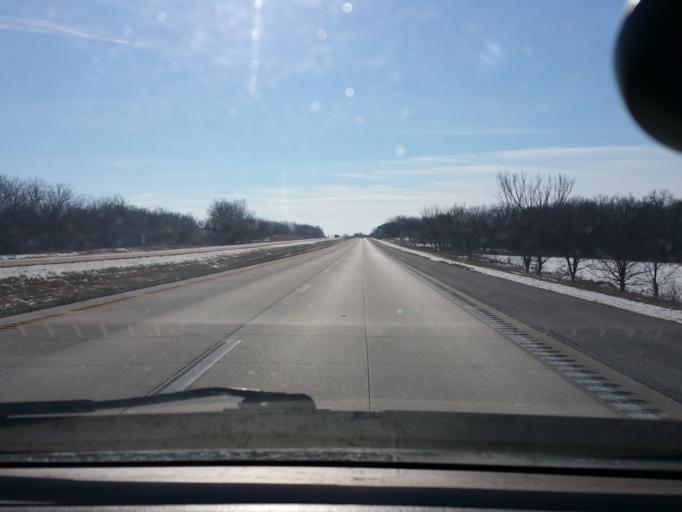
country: US
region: Missouri
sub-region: Daviess County
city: Gallatin
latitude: 40.0163
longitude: -94.0963
